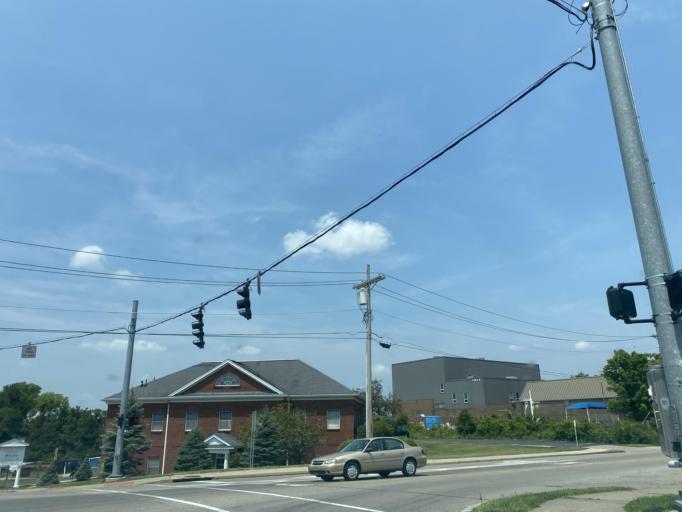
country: US
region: Kentucky
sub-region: Campbell County
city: Fort Thomas
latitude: 39.0593
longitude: -84.4515
